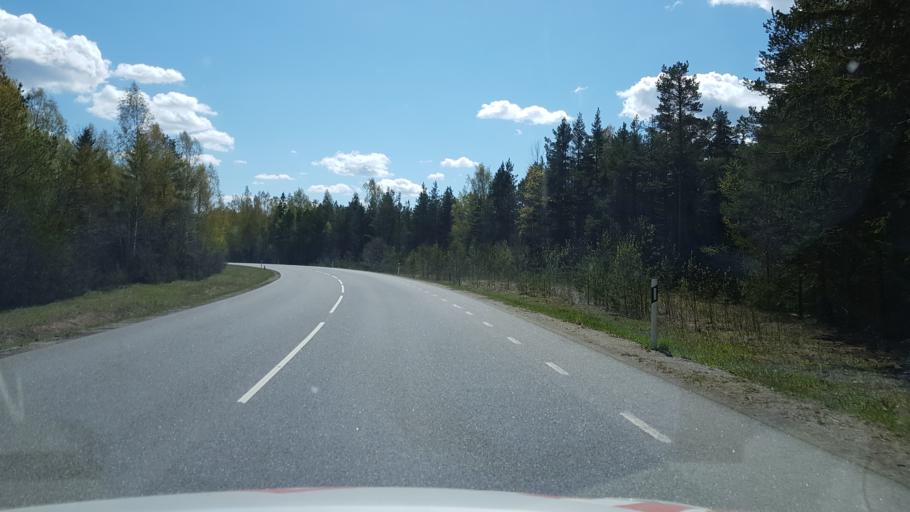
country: EE
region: Harju
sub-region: Paldiski linn
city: Paldiski
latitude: 59.2759
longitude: 24.1312
